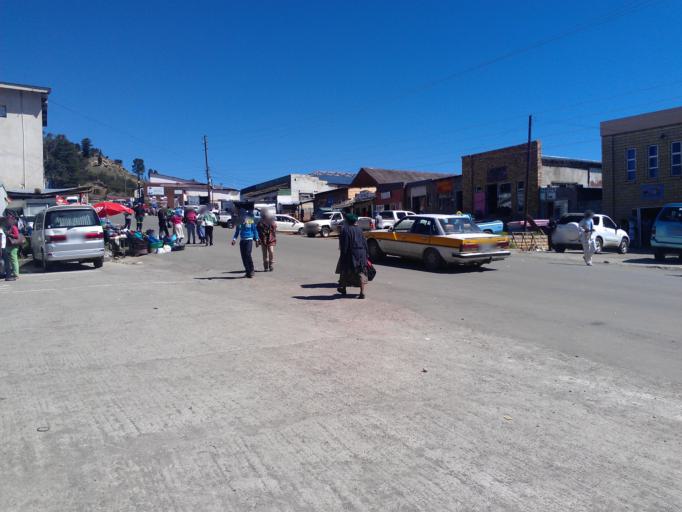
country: LS
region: Qacha's Nek
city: Qacha's Nek
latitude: -30.1184
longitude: 28.6849
